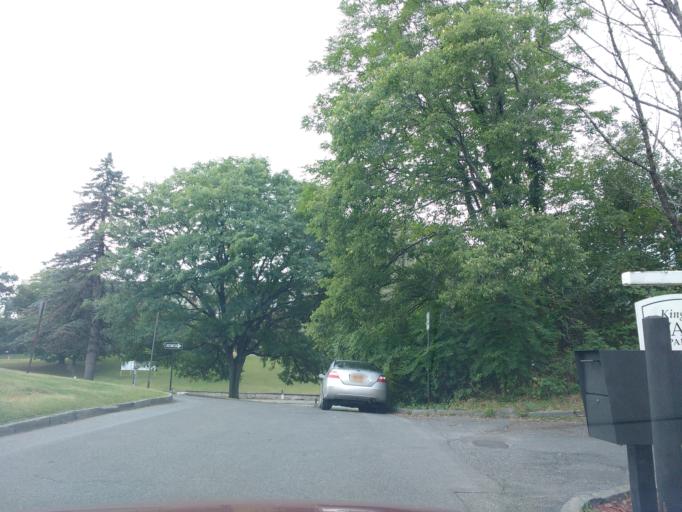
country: US
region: New York
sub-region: Ulster County
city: Kingston
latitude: 41.9273
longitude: -73.9968
